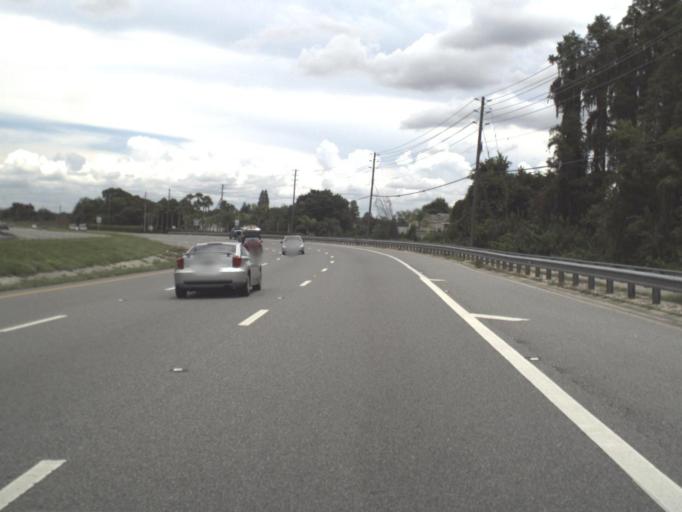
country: US
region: Florida
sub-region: Pasco County
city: Land O' Lakes
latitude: 28.1863
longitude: -82.4520
